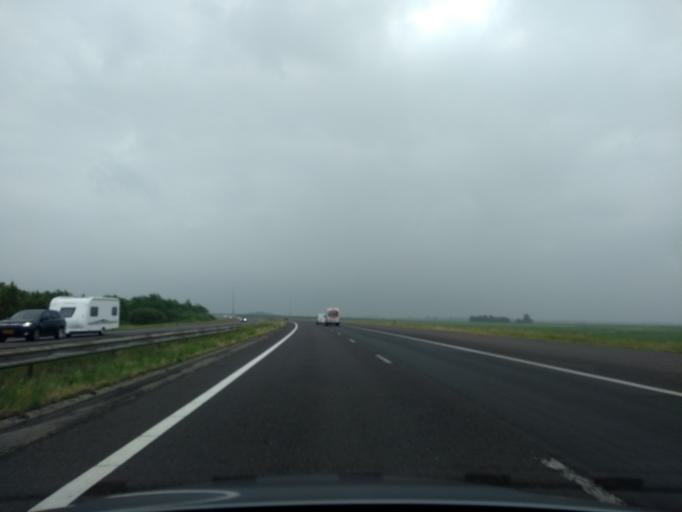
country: NL
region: Friesland
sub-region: Sudwest Fryslan
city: Oppenhuizen
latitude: 52.9916
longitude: 5.7158
